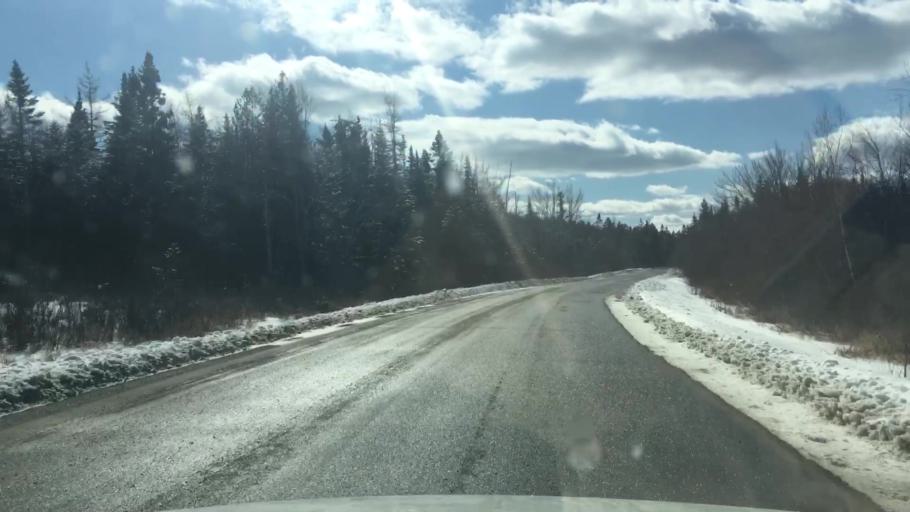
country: US
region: Maine
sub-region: Washington County
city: Machiasport
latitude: 44.6773
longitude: -67.4167
